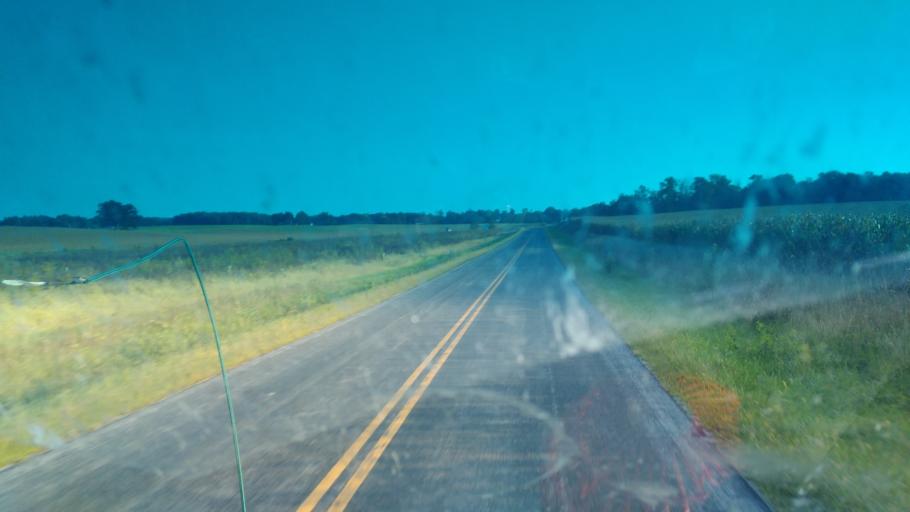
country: US
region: Ohio
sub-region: Crawford County
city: Bucyrus
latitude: 40.8821
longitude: -82.8765
